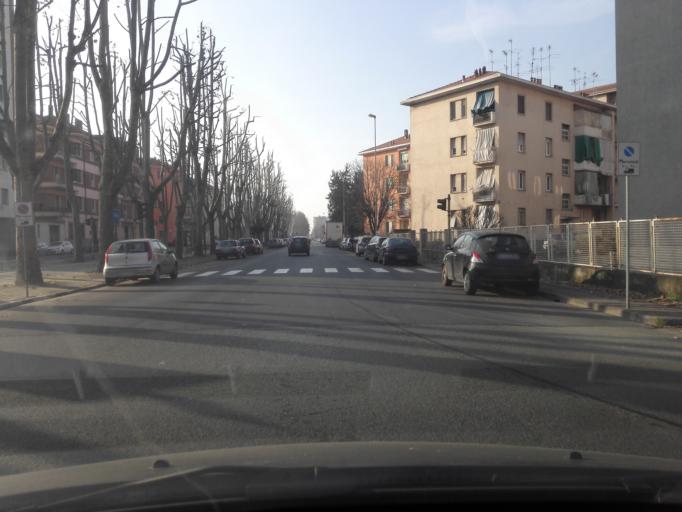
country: IT
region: Piedmont
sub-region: Provincia di Alessandria
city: Alessandria
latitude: 44.9082
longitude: 8.6242
